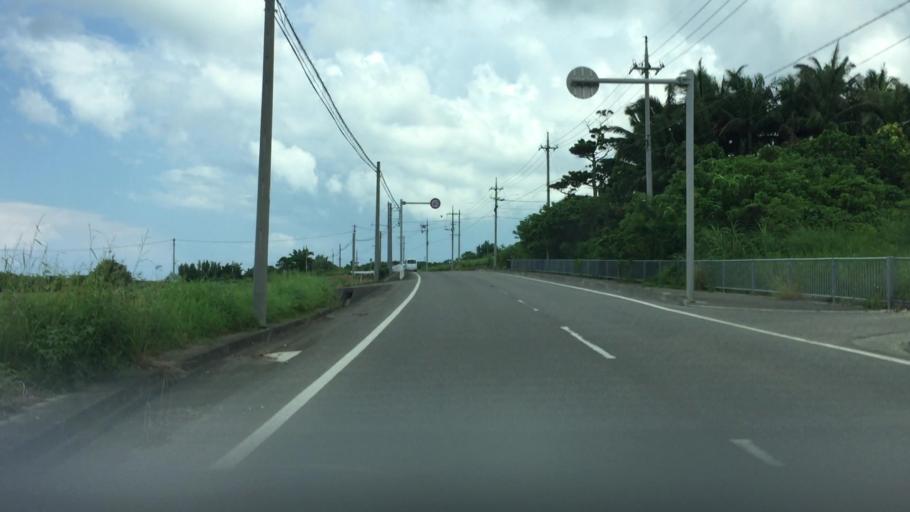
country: JP
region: Okinawa
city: Ishigaki
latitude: 24.3670
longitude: 124.1380
